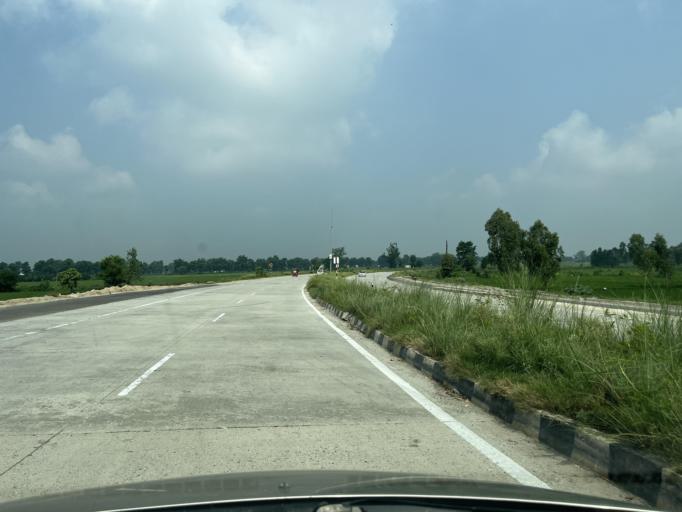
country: IN
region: Uttarakhand
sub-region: Udham Singh Nagar
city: Kashipur
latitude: 29.1763
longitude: 78.9411
